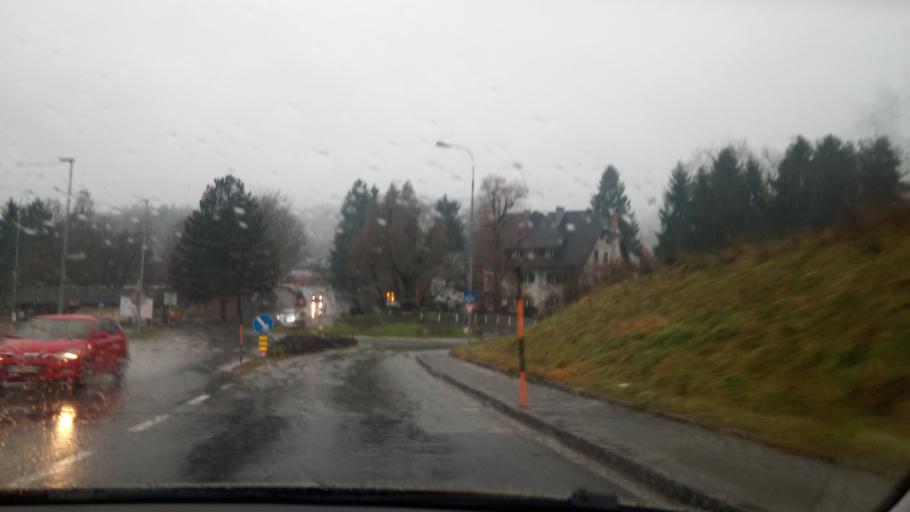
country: AT
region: Carinthia
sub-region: Politischer Bezirk Klagenfurt Land
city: Keutschach am See
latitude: 46.5920
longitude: 14.1702
